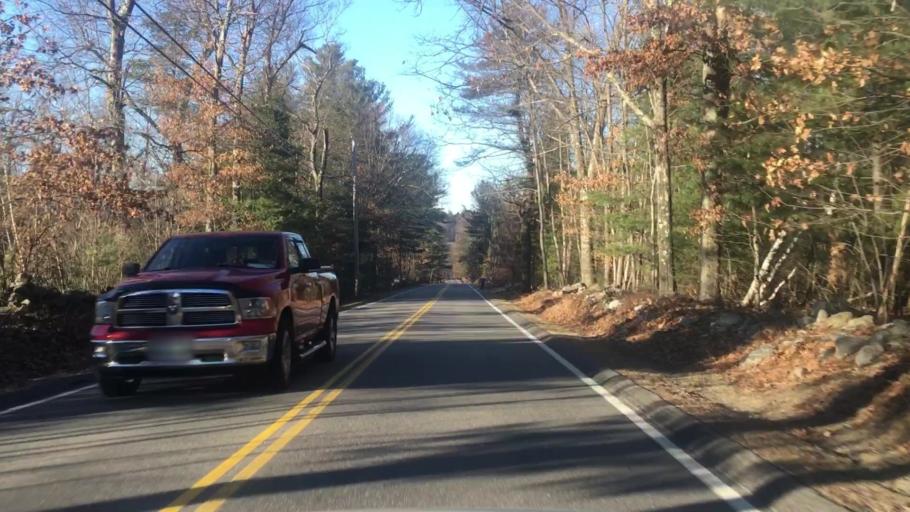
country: US
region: New Hampshire
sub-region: Rockingham County
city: Londonderry
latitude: 42.8913
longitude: -71.3695
